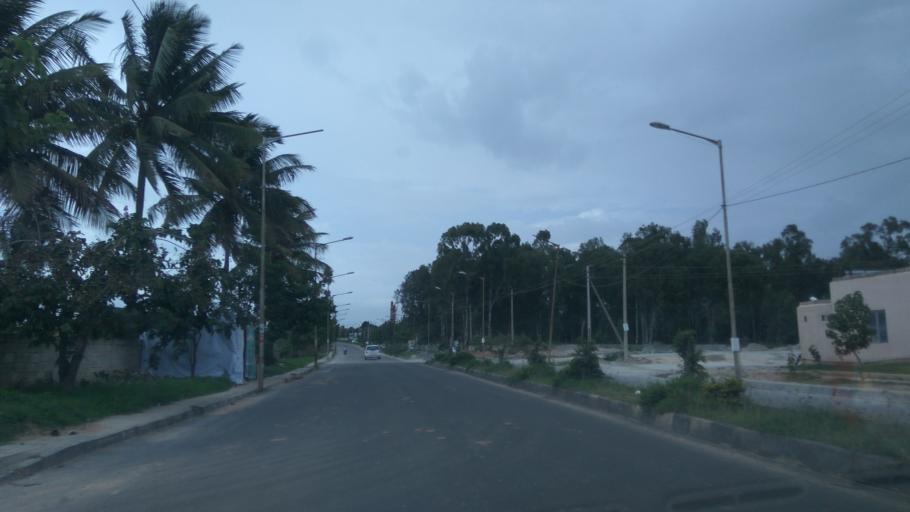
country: IN
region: Karnataka
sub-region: Bangalore Urban
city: Yelahanka
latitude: 13.0942
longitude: 77.6359
